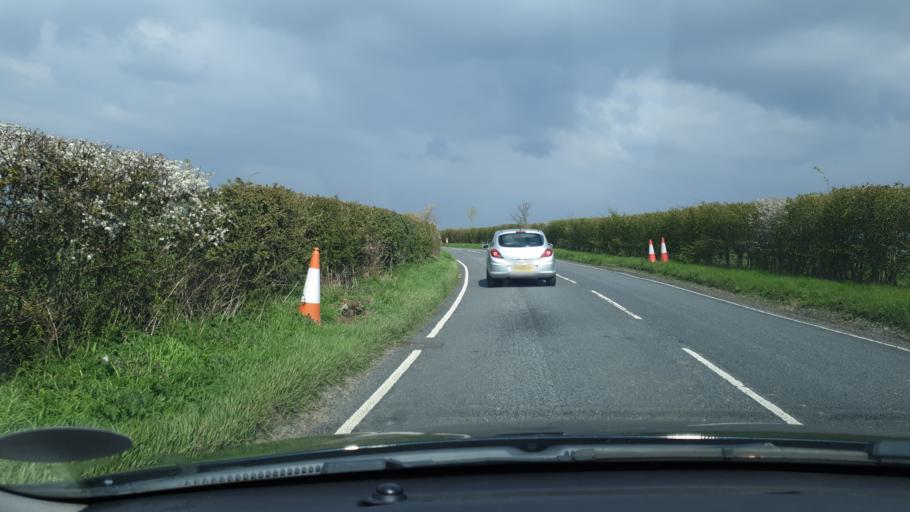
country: GB
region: England
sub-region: Essex
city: Mistley
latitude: 51.8984
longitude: 1.0909
